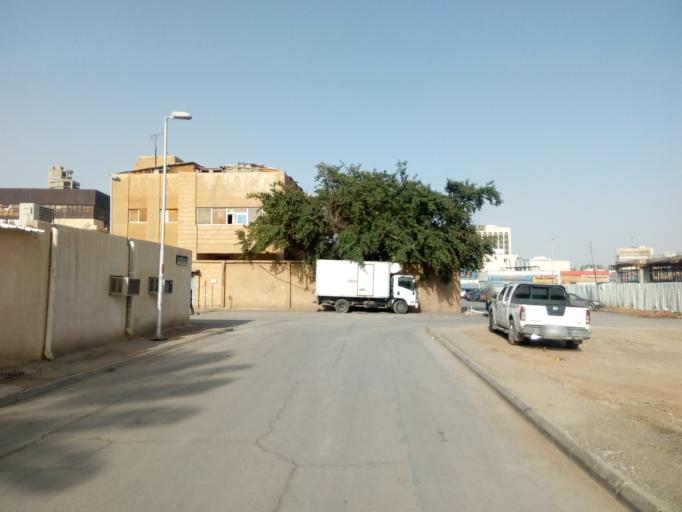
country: SA
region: Ar Riyad
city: Riyadh
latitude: 24.6507
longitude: 46.7080
